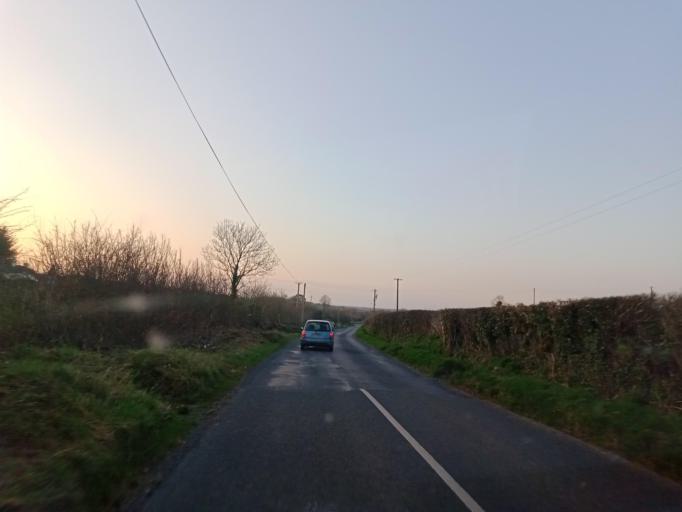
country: IE
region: Leinster
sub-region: Kilkenny
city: Castlecomer
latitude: 52.8493
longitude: -7.2597
